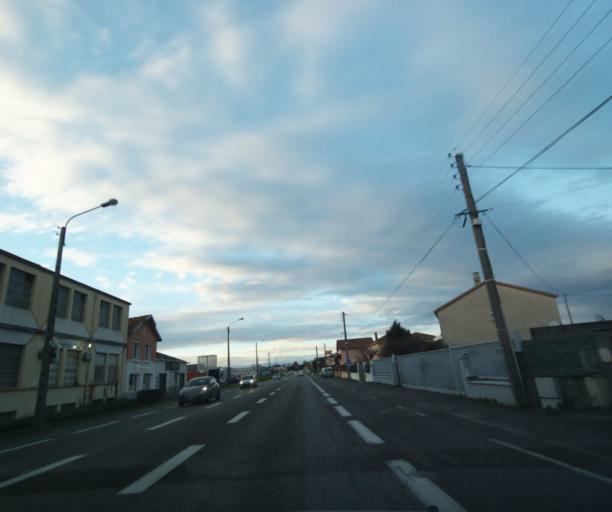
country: FR
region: Rhone-Alpes
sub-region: Departement de la Drome
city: Bourg-les-Valence
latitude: 44.9545
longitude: 4.8906
